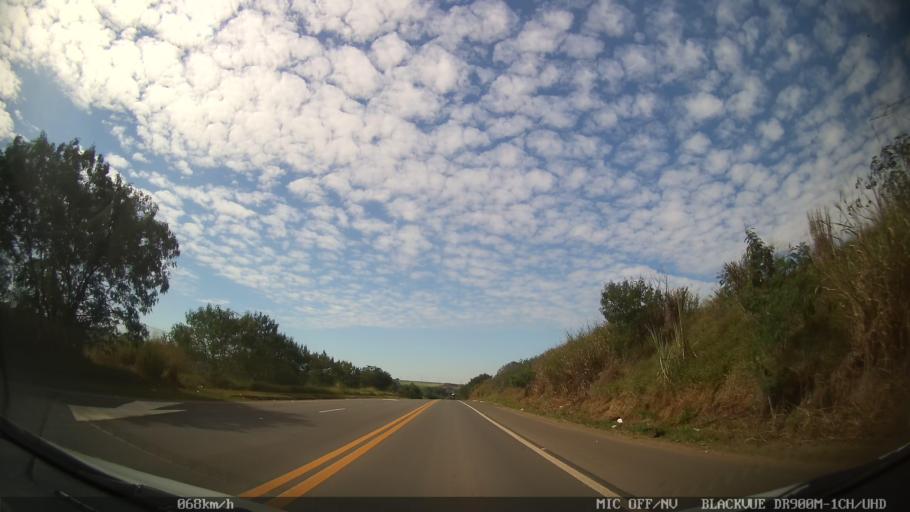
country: BR
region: Sao Paulo
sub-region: Santa Barbara D'Oeste
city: Santa Barbara d'Oeste
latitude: -22.7057
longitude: -47.4465
